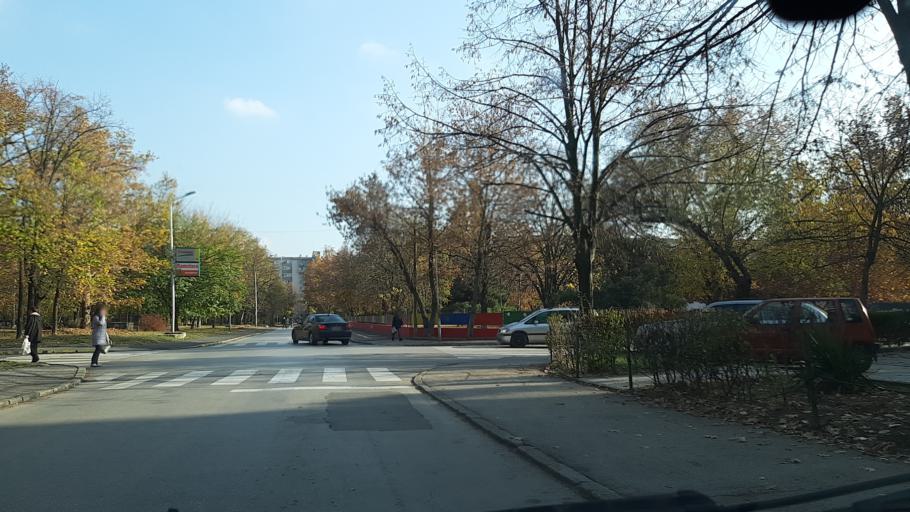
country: MK
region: Karpos
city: Skopje
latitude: 41.9871
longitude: 21.4579
